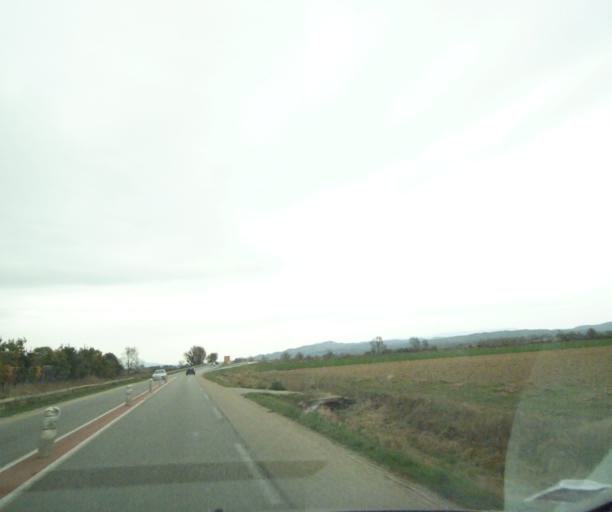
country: FR
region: Provence-Alpes-Cote d'Azur
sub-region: Departement des Bouches-du-Rhone
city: Le Puy-Sainte-Reparade
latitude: 43.6618
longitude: 5.4714
